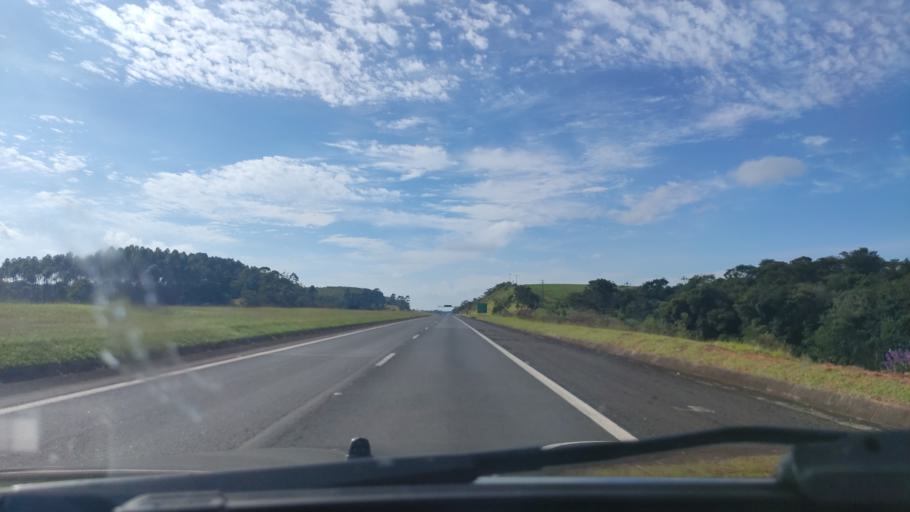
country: BR
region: Sao Paulo
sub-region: Itatinga
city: Itatinga
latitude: -23.0681
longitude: -48.5493
